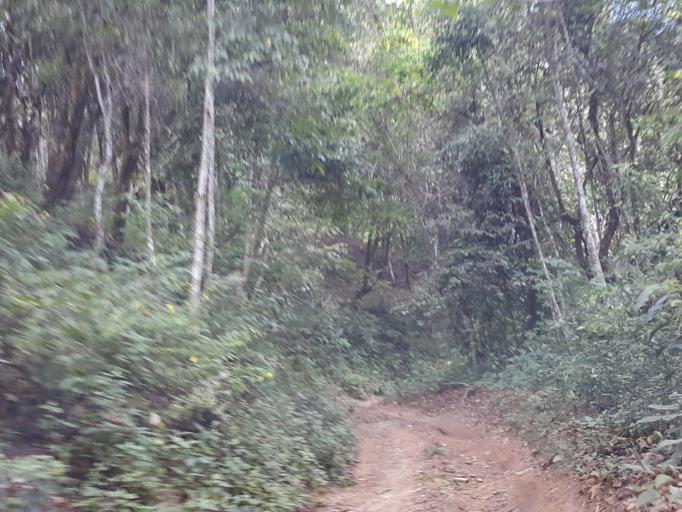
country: TH
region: Chiang Mai
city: Wiang Haeng
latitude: 19.5528
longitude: 98.8143
